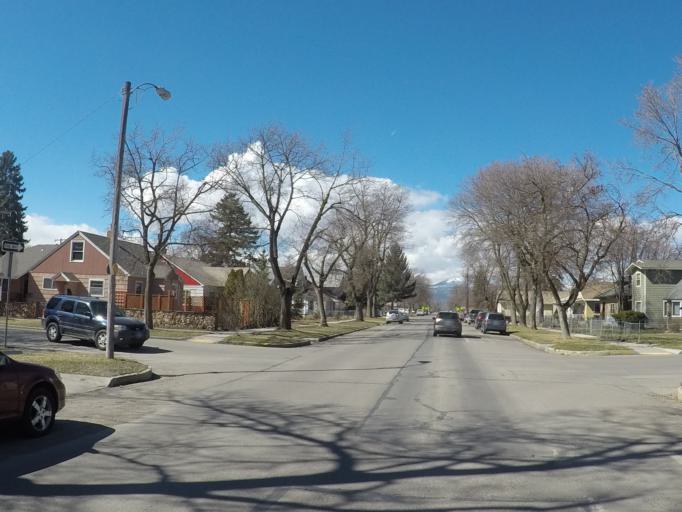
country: US
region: Montana
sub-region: Missoula County
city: Missoula
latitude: 46.8651
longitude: -114.0078
